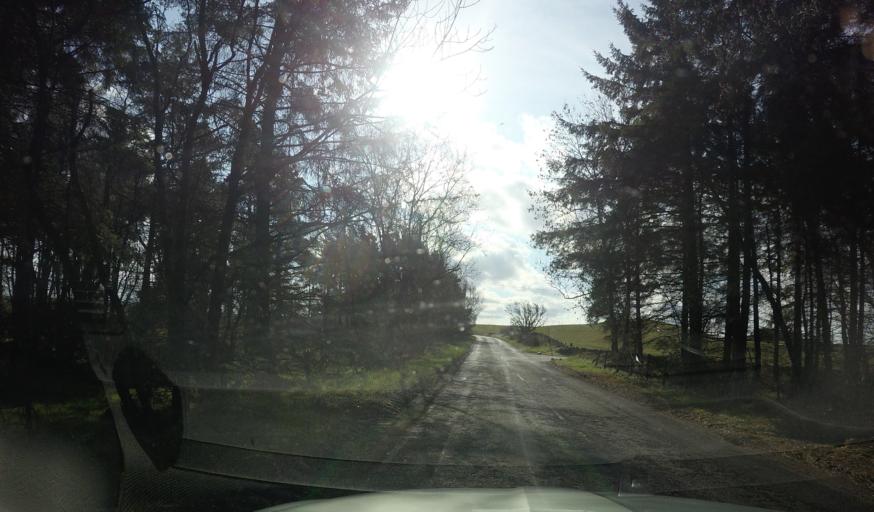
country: GB
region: Scotland
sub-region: Midlothian
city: Penicuik
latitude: 55.8137
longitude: -3.1927
